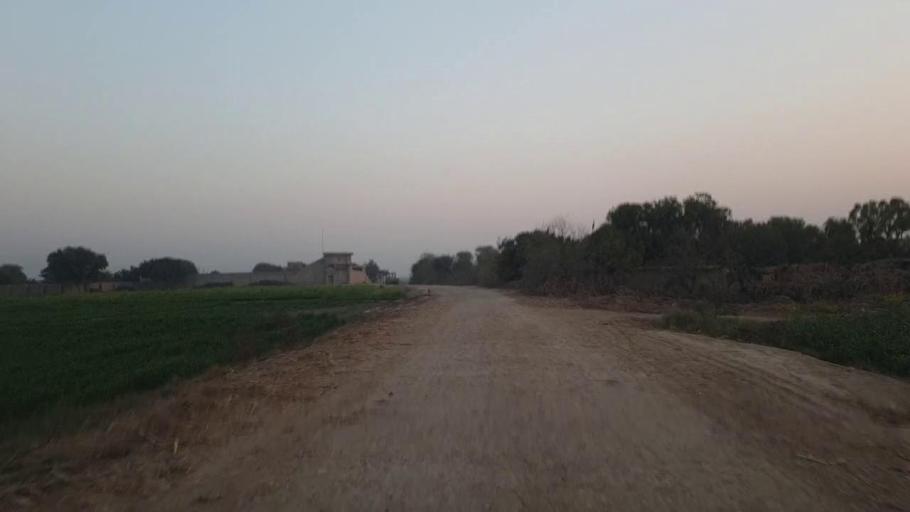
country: PK
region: Sindh
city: Tando Allahyar
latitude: 25.4450
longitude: 68.7645
